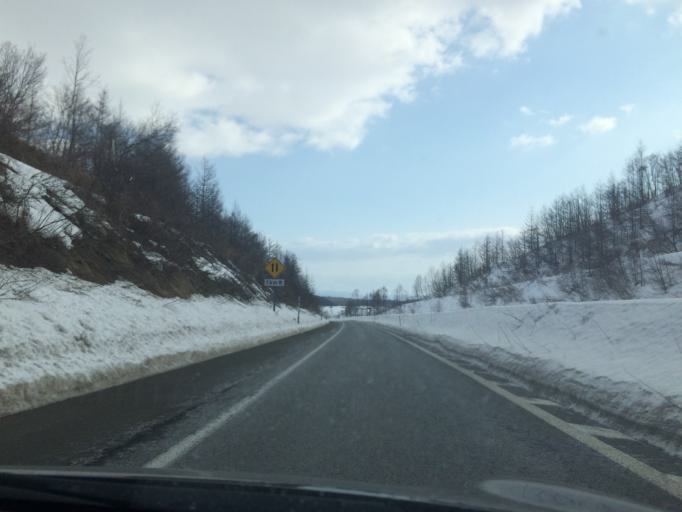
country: JP
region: Hokkaido
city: Chitose
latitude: 42.8776
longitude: 141.7447
